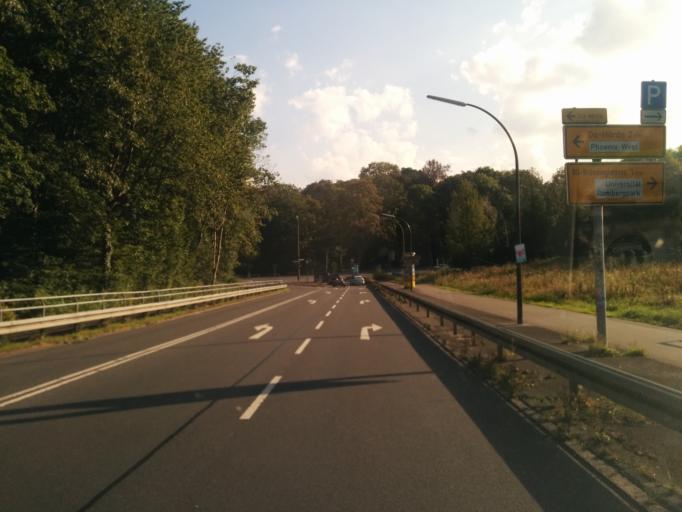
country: DE
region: North Rhine-Westphalia
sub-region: Regierungsbezirk Arnsberg
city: Dortmund
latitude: 51.4851
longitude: 7.4680
